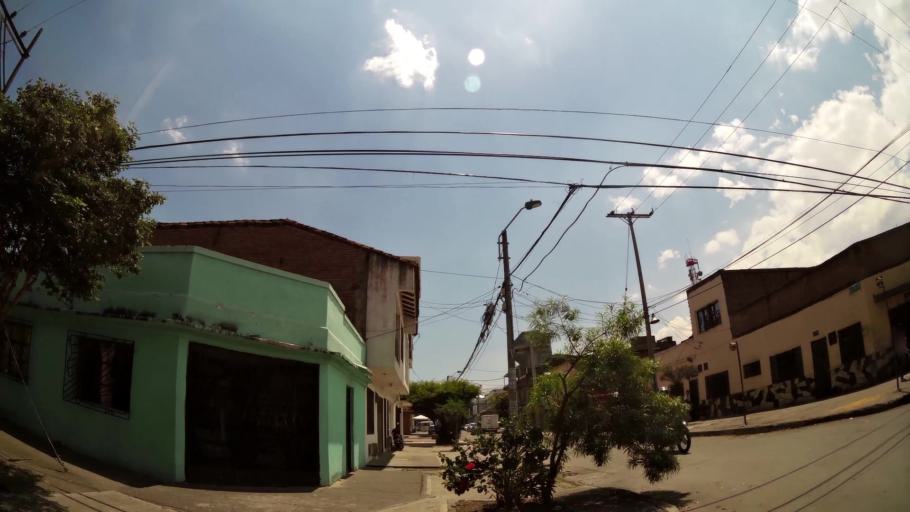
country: CO
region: Valle del Cauca
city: Cali
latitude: 3.4457
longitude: -76.5001
